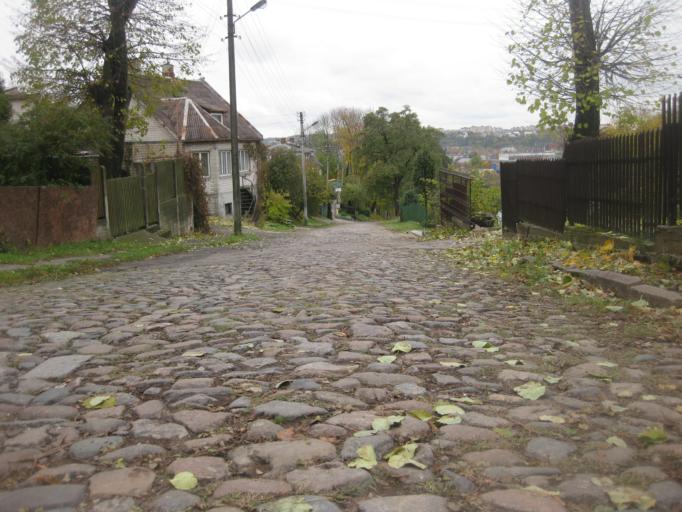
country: LT
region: Kauno apskritis
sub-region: Kaunas
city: Kaunas
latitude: 54.9087
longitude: 23.9115
